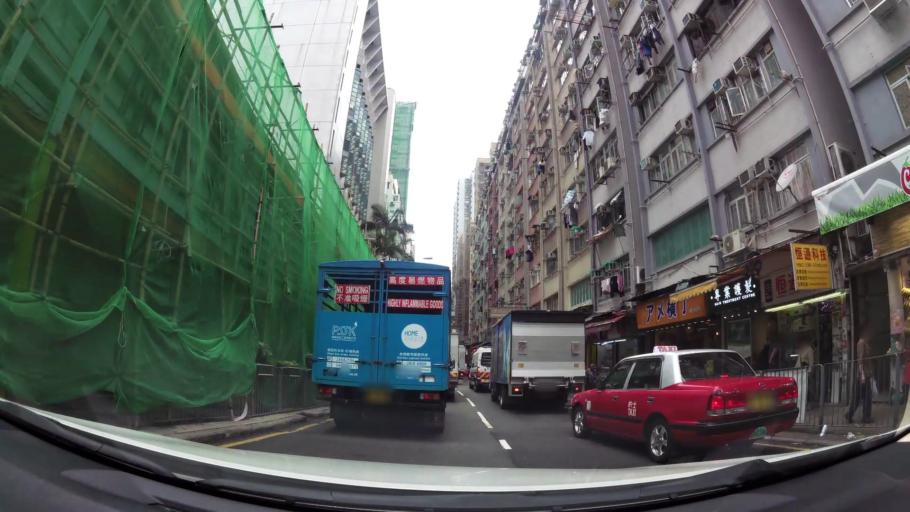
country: HK
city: Hong Kong
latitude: 22.2858
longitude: 114.1367
